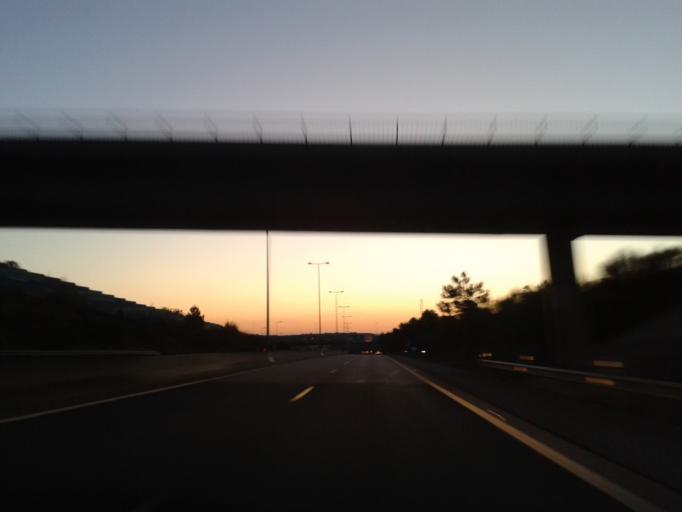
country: PT
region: Faro
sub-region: Albufeira
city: Guia
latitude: 37.1394
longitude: -8.3276
